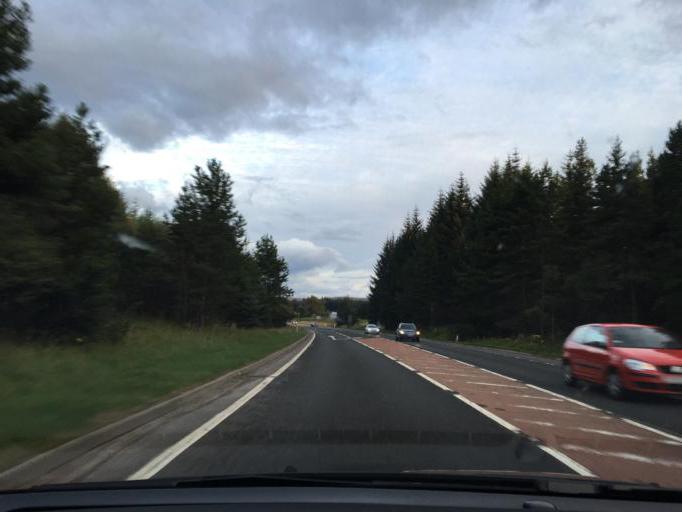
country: GB
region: Scotland
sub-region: Highland
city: Aviemore
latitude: 57.3478
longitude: -4.0053
